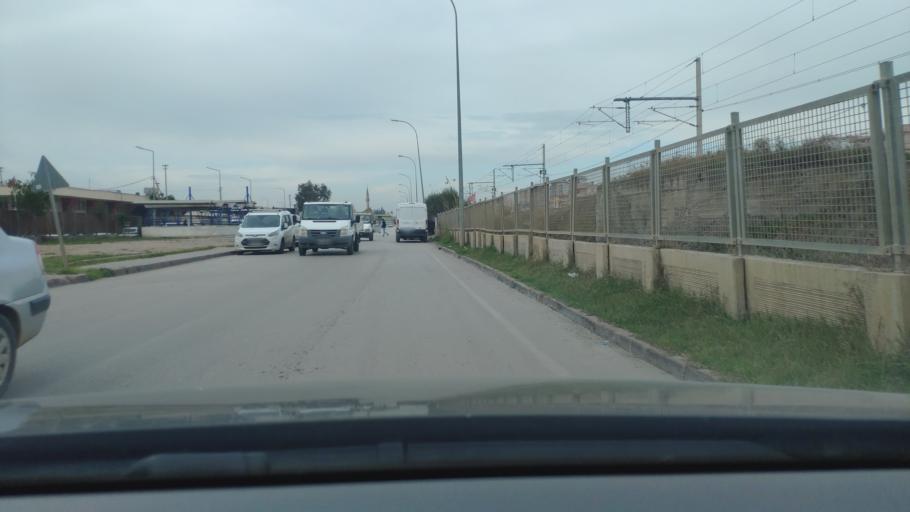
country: TR
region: Adana
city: Seyhan
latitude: 36.9979
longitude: 35.2662
